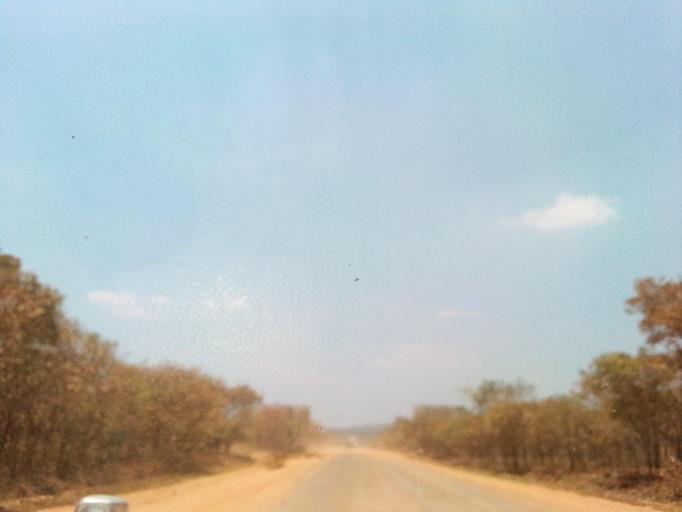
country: ZM
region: Northern
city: Mpika
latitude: -12.2112
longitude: 31.1738
